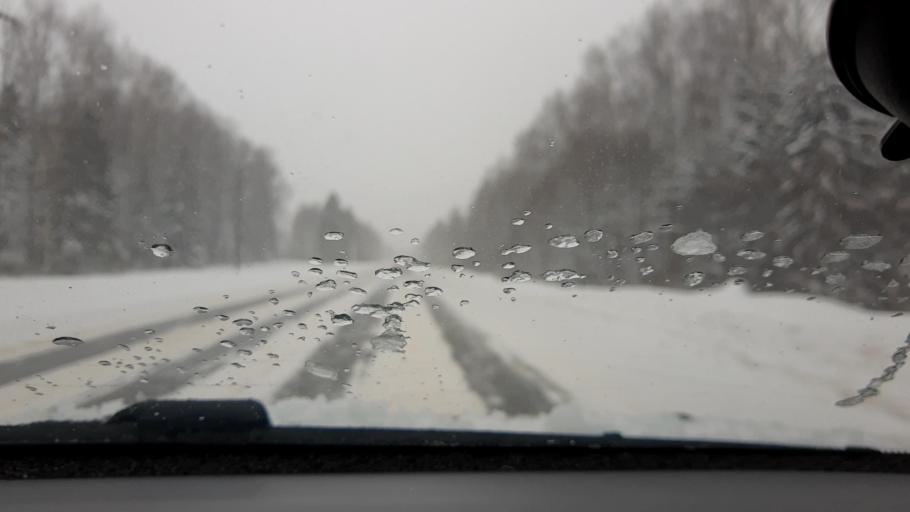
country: RU
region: Nizjnij Novgorod
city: Purekh
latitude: 56.6323
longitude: 43.1679
